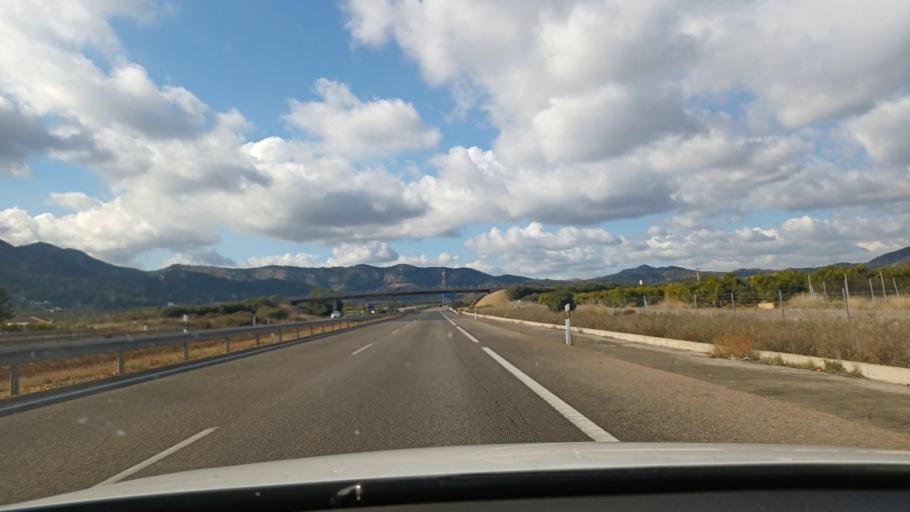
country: ES
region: Valencia
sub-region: Provincia de Castello
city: Villavieja
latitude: 39.8677
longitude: -0.1779
